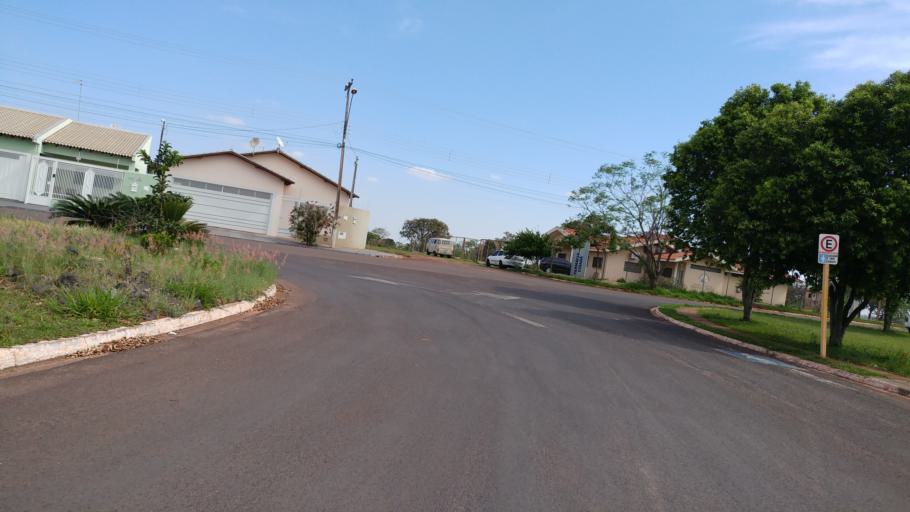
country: BR
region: Sao Paulo
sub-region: Paraguacu Paulista
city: Paraguacu Paulista
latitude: -22.4062
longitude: -50.5842
